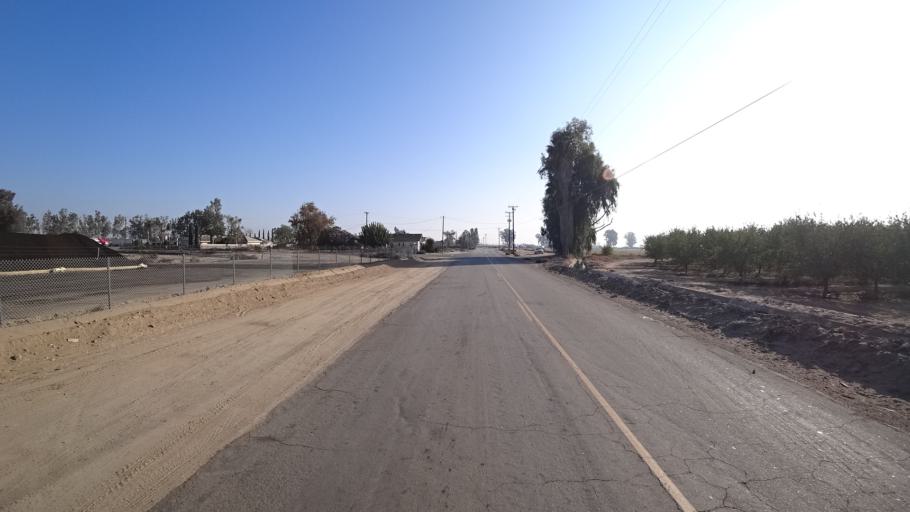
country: US
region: California
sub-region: Kern County
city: Greenfield
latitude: 35.2597
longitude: -119.0266
